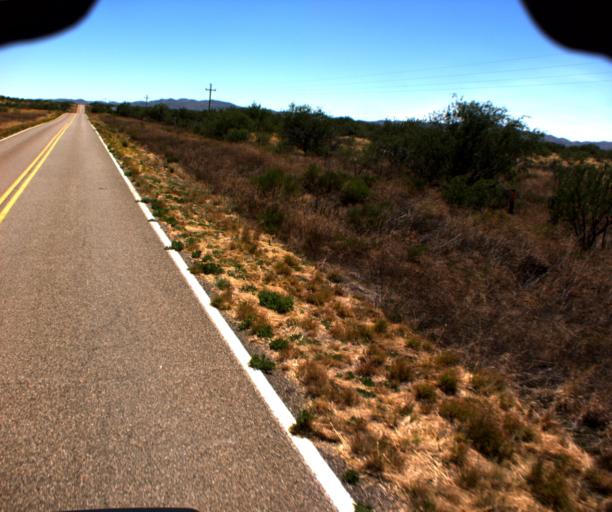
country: US
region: Arizona
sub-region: Pima County
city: Arivaca Junction
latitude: 31.6188
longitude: -111.5146
